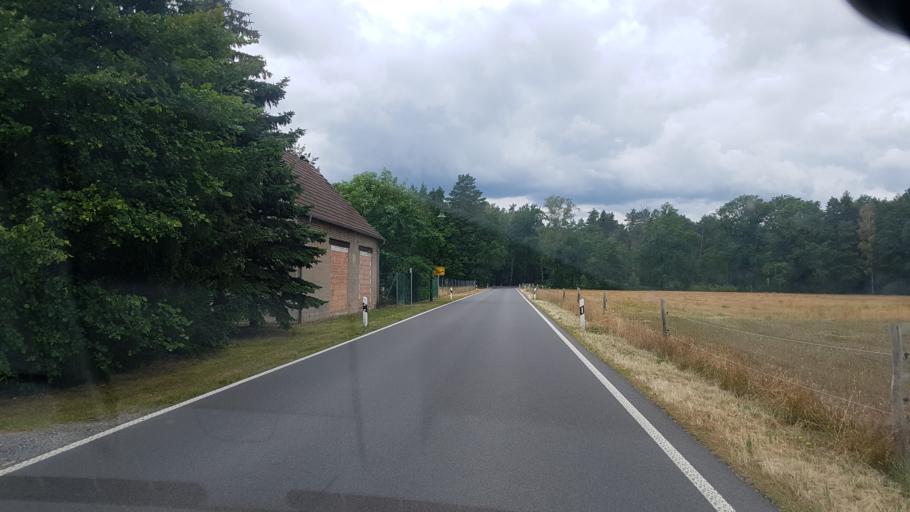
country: DE
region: Saxony
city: Mucka
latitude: 51.3776
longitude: 14.7119
